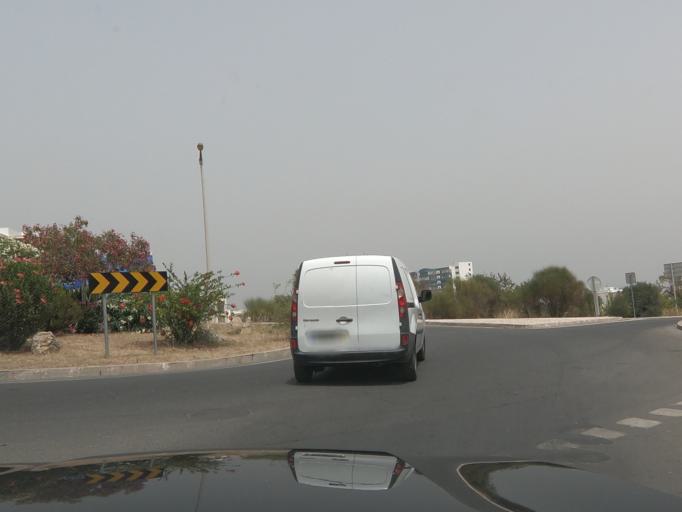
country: PT
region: Faro
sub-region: Portimao
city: Portimao
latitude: 37.1269
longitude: -8.5429
